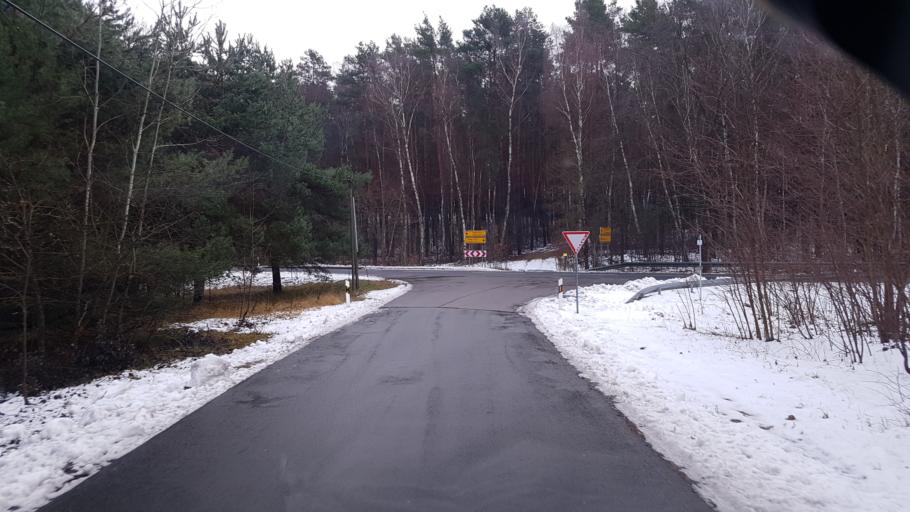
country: DE
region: Brandenburg
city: Lieberose
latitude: 51.9725
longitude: 14.2029
